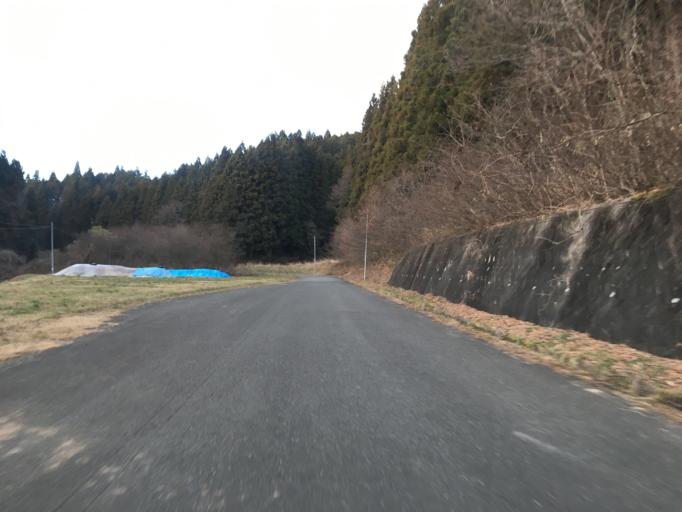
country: JP
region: Fukushima
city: Ishikawa
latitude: 37.1882
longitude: 140.5917
